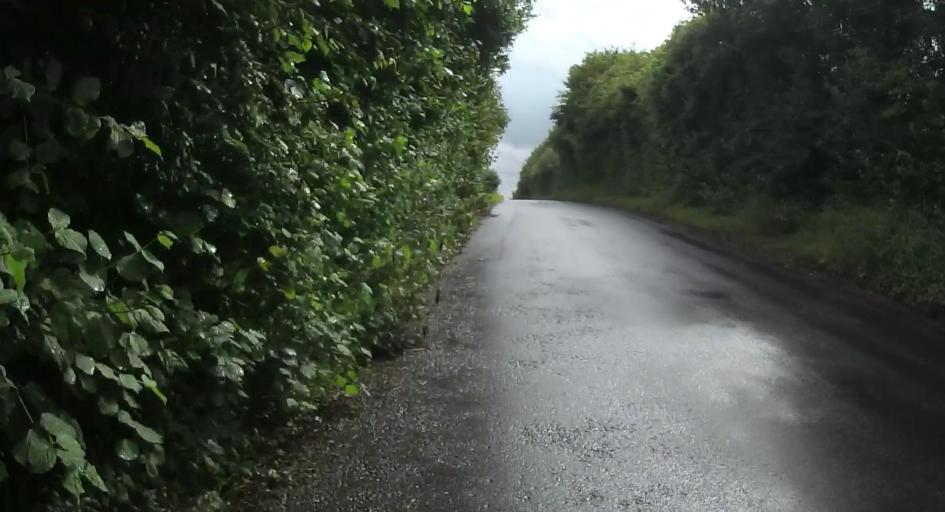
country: GB
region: England
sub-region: Hampshire
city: Andover
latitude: 51.2164
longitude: -1.4441
